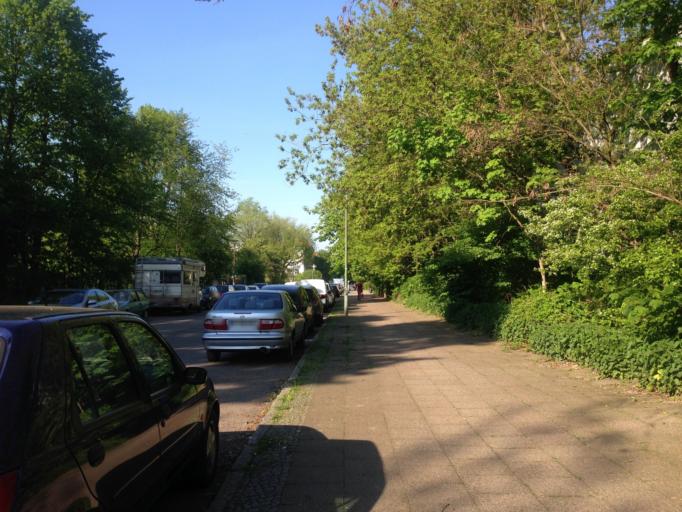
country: DE
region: Berlin
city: Pankow
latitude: 52.5744
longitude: 13.4149
